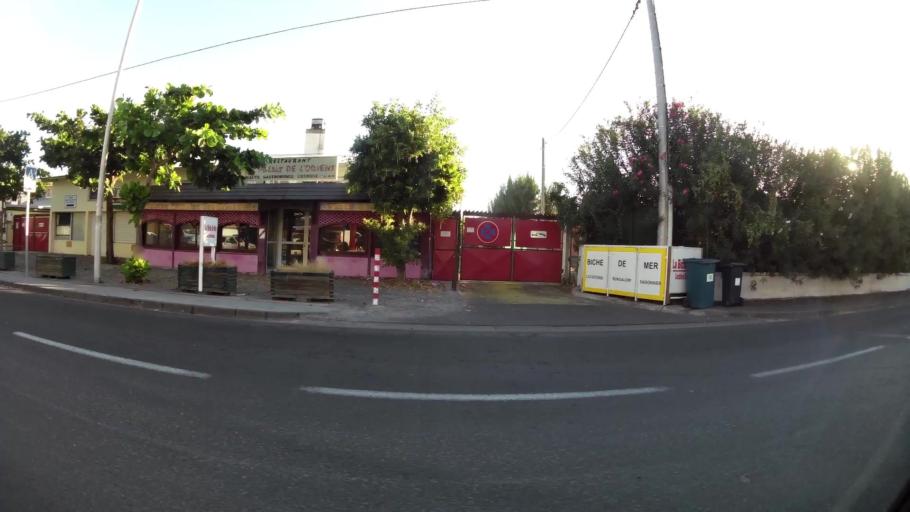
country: RE
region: Reunion
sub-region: Reunion
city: Trois-Bassins
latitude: -21.0929
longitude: 55.2361
